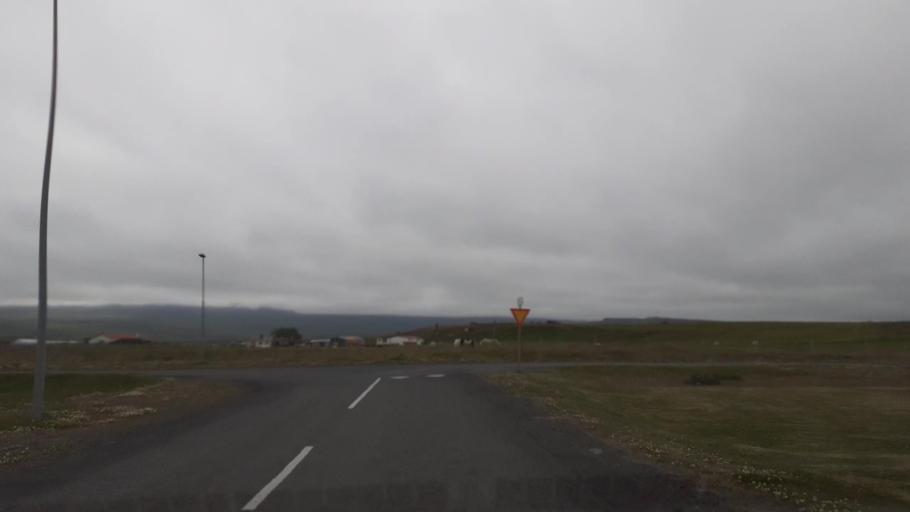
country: IS
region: Northwest
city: Saudarkrokur
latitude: 65.6557
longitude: -20.3037
